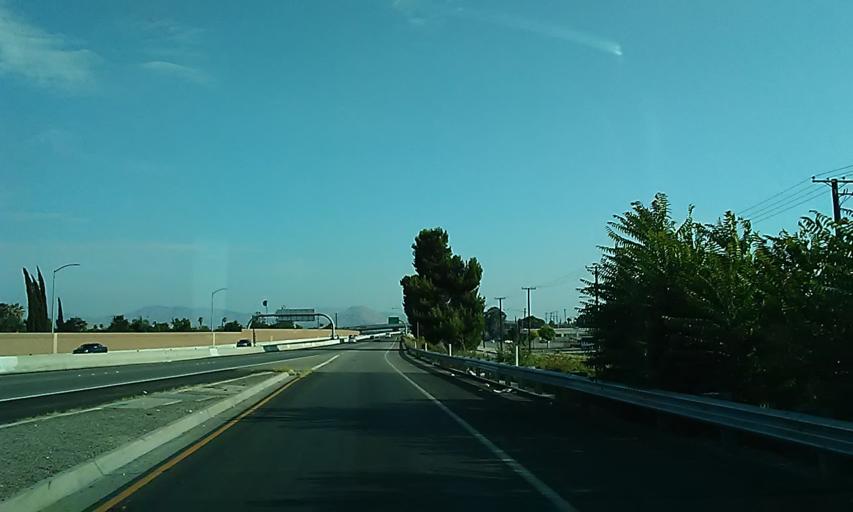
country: US
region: California
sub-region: San Bernardino County
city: San Bernardino
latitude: 34.1345
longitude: -117.3030
